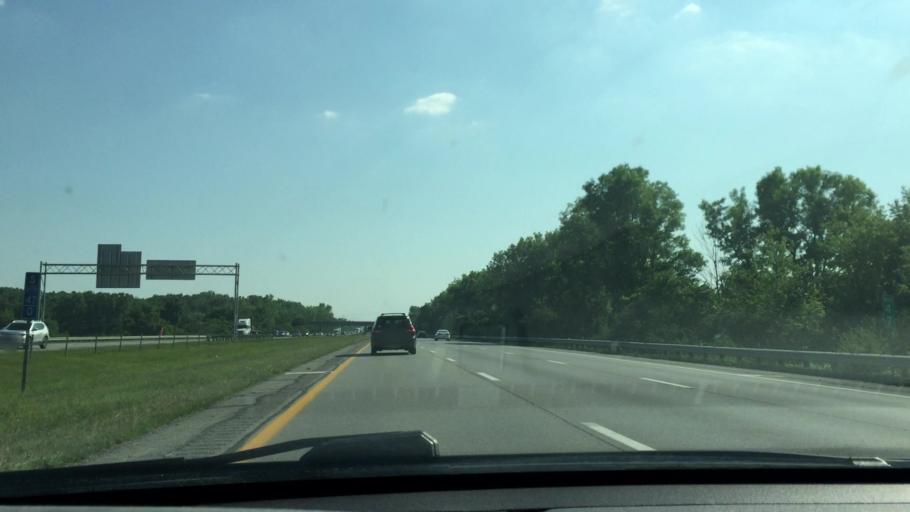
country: US
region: Ohio
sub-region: Franklin County
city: Groveport
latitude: 39.8925
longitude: -82.9079
